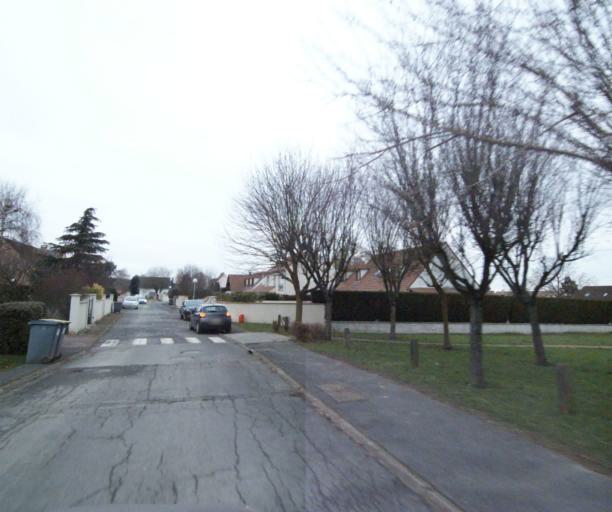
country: FR
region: Ile-de-France
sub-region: Departement de Seine-et-Marne
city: Dammartin-en-Goele
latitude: 49.0602
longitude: 2.6840
